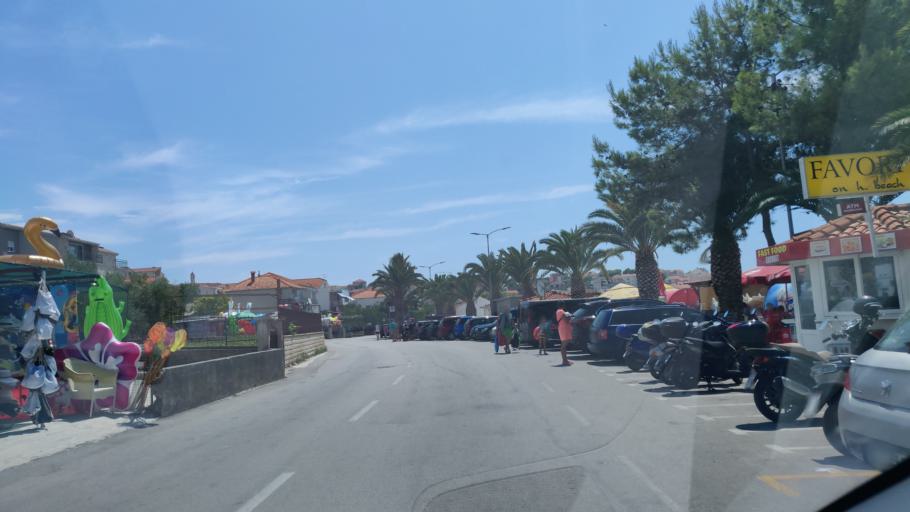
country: HR
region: Splitsko-Dalmatinska
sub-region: Grad Trogir
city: Trogir
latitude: 43.4988
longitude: 16.2602
